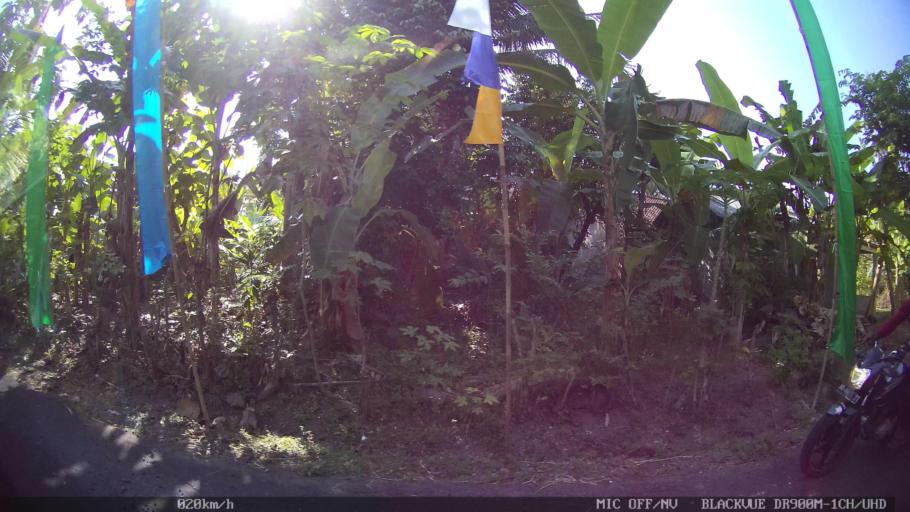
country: ID
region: Daerah Istimewa Yogyakarta
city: Kasihan
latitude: -7.8280
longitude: 110.2883
